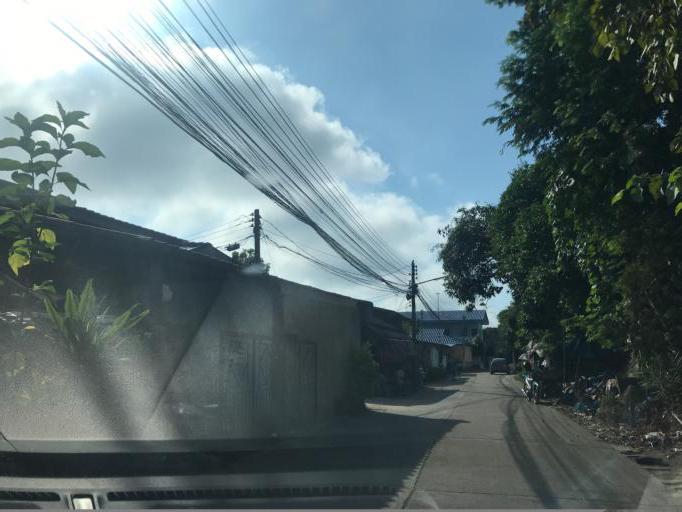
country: TH
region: Chiang Mai
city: San Sai
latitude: 18.8282
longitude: 99.0220
